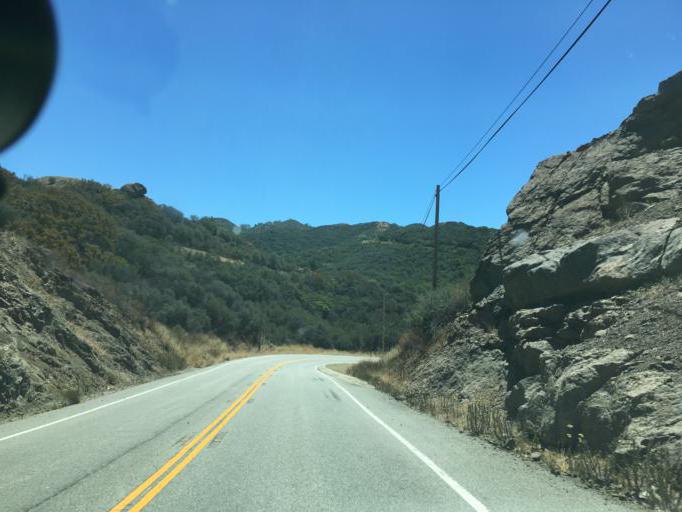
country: US
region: California
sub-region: Los Angeles County
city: Westlake Village
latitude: 34.0895
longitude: -118.8390
